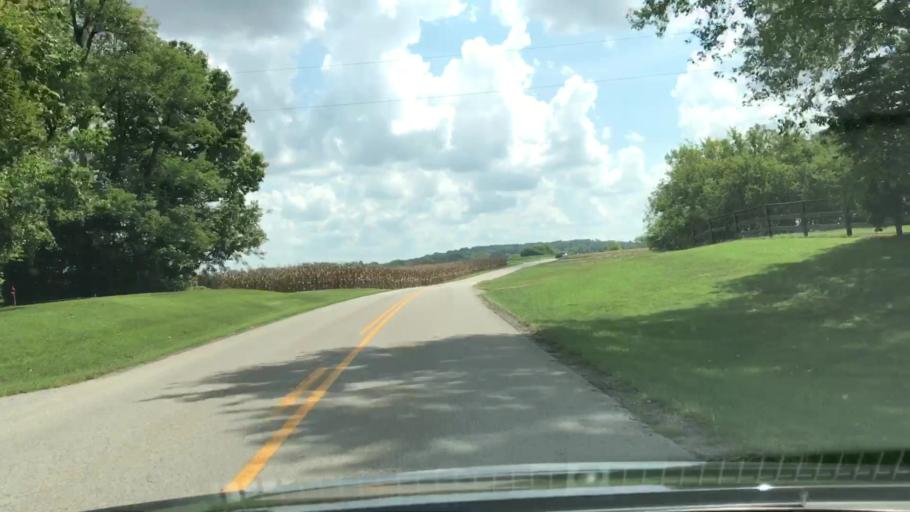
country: US
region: Kentucky
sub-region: Todd County
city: Guthrie
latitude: 36.7093
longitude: -87.0499
